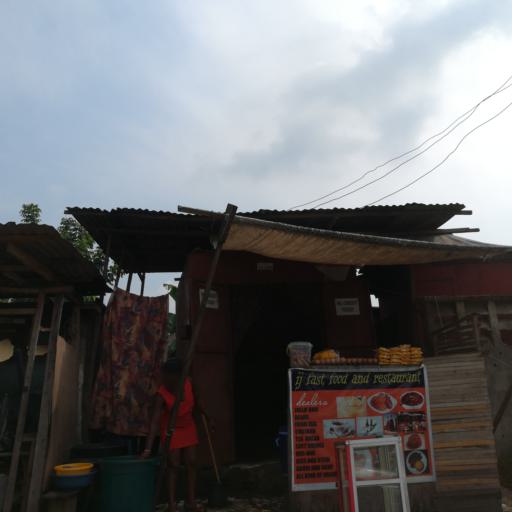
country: NG
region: Rivers
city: Port Harcourt
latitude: 4.8408
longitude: 7.0661
